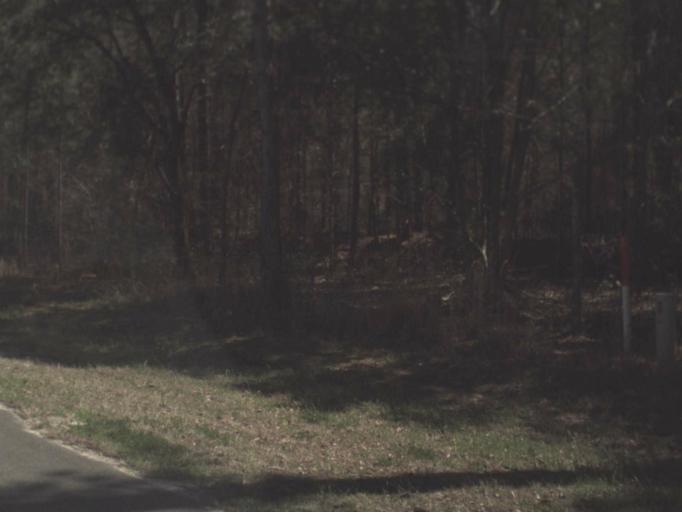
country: US
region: Florida
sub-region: Gadsden County
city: Gretna
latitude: 30.5928
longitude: -84.6634
